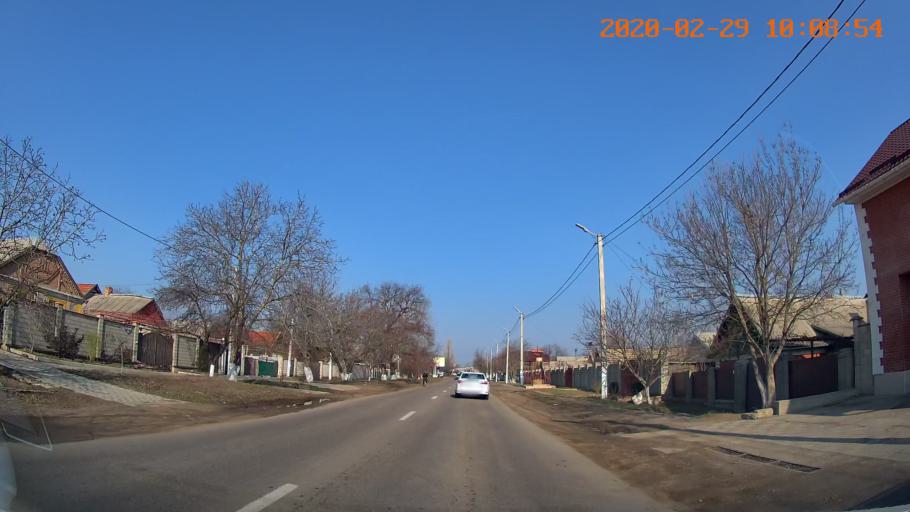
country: MD
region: Telenesti
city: Tiraspolul Nou
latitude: 46.8250
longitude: 29.6552
